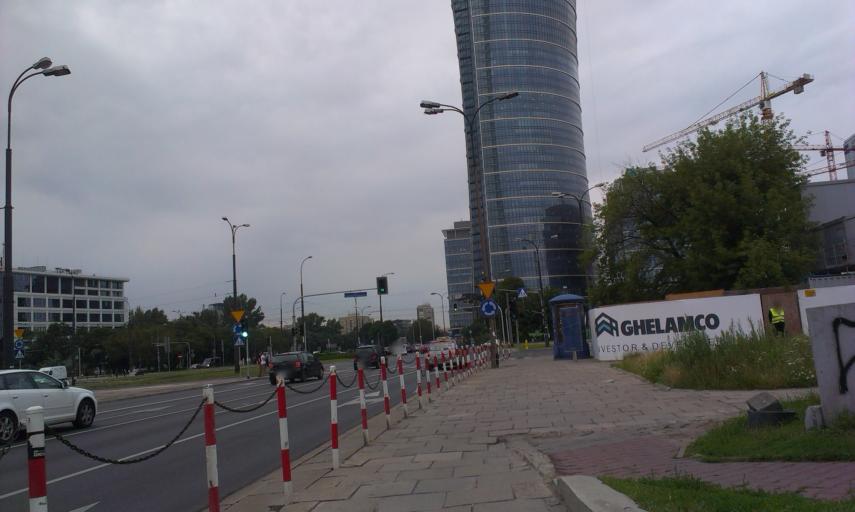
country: PL
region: Masovian Voivodeship
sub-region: Warszawa
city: Ochota
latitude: 52.2297
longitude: 20.9855
